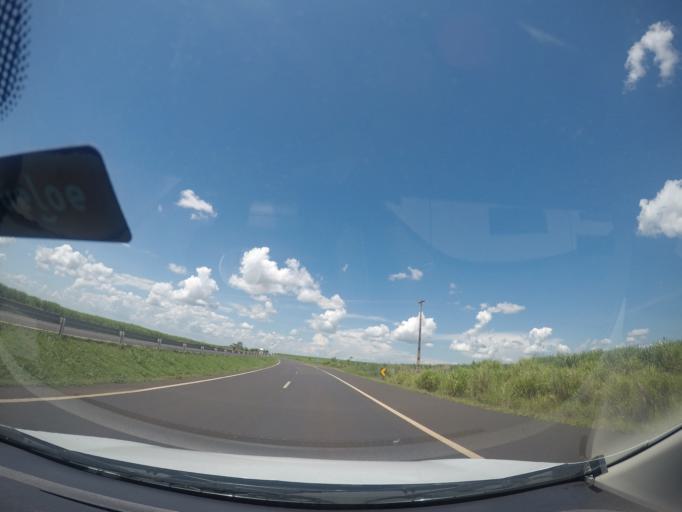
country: BR
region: Minas Gerais
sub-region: Prata
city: Prata
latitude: -19.6533
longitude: -48.8223
